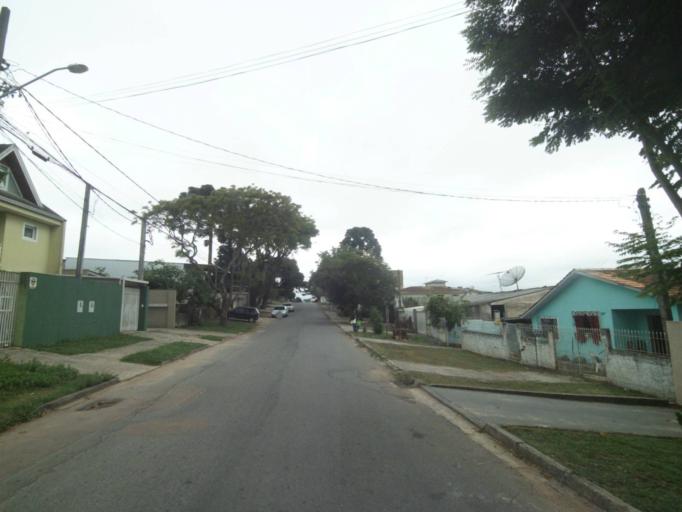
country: BR
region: Parana
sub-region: Sao Jose Dos Pinhais
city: Sao Jose dos Pinhais
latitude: -25.5421
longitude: -49.2930
